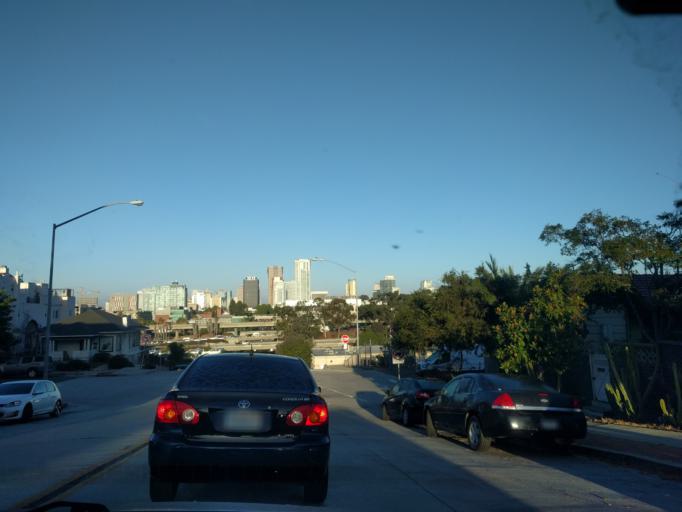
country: US
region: California
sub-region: San Diego County
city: San Diego
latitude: 32.7179
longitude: -117.1446
